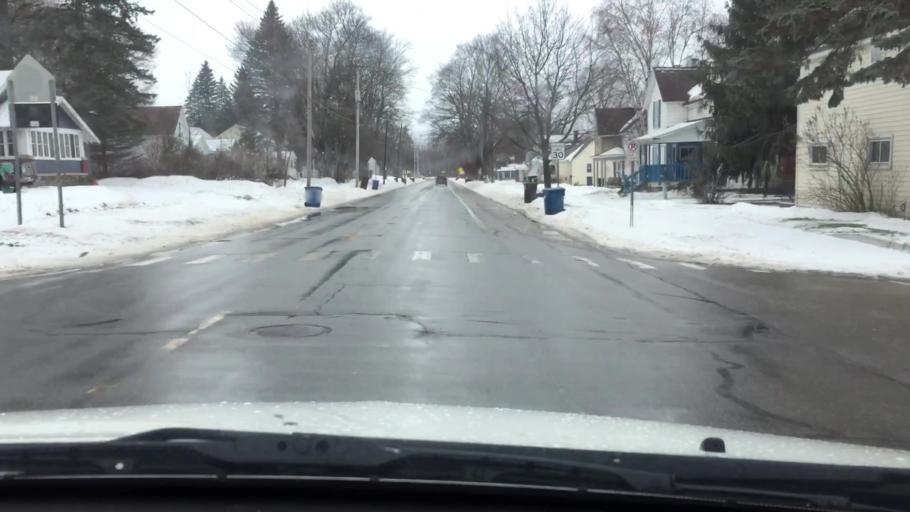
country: US
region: Michigan
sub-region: Wexford County
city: Cadillac
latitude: 44.2410
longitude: -85.4011
